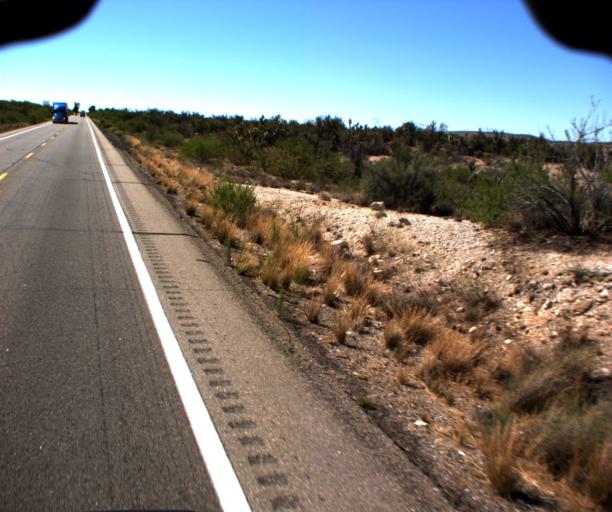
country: US
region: Arizona
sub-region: Yavapai County
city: Bagdad
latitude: 34.3090
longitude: -113.1255
